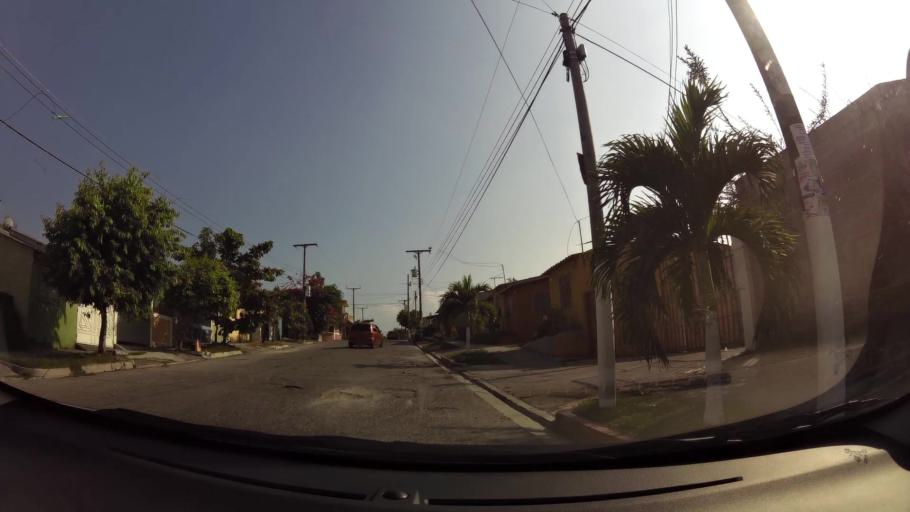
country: SV
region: San Salvador
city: Ilopango
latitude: 13.7280
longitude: -89.1117
